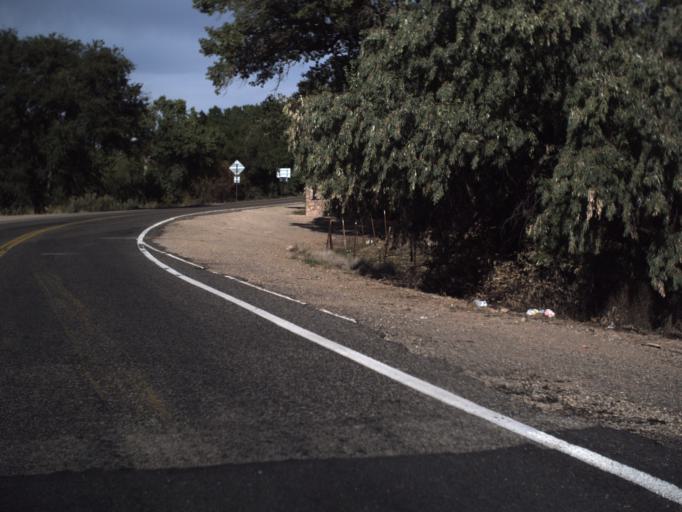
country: US
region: Utah
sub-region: Washington County
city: Toquerville
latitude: 37.2288
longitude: -113.3733
